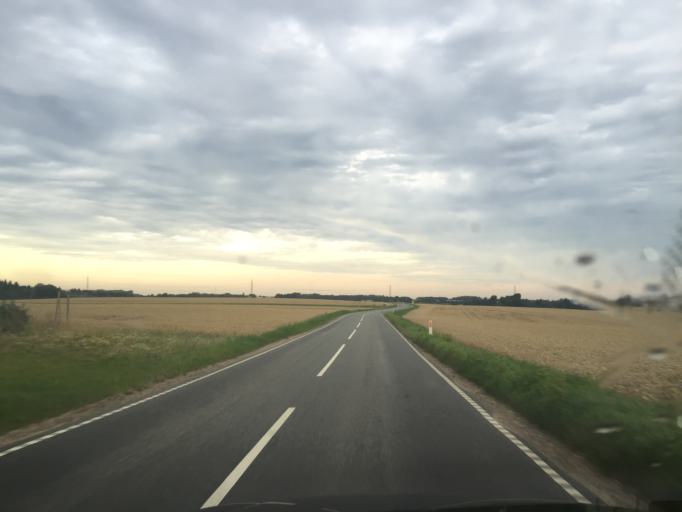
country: DK
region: Capital Region
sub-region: Egedal Kommune
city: Vekso
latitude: 55.6930
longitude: 12.2428
